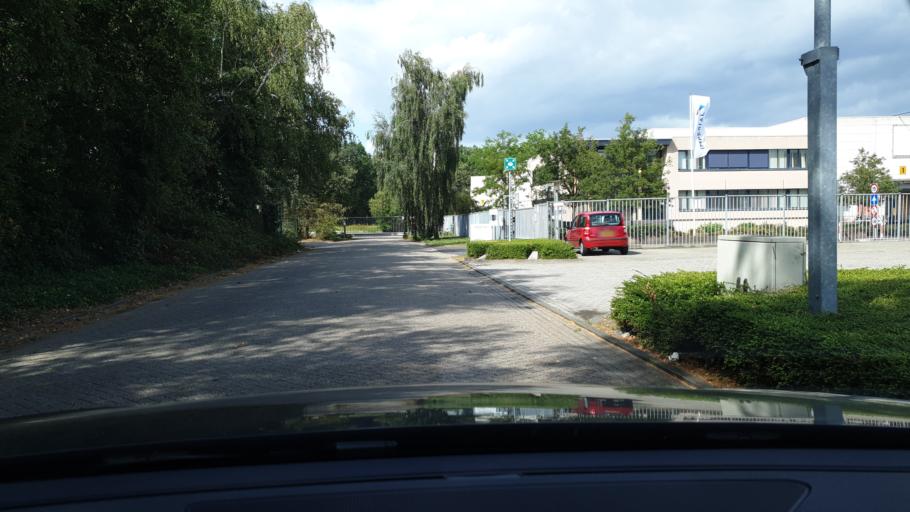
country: NL
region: North Brabant
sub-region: Gemeente Son en Breugel
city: Son
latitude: 51.5022
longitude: 5.4590
